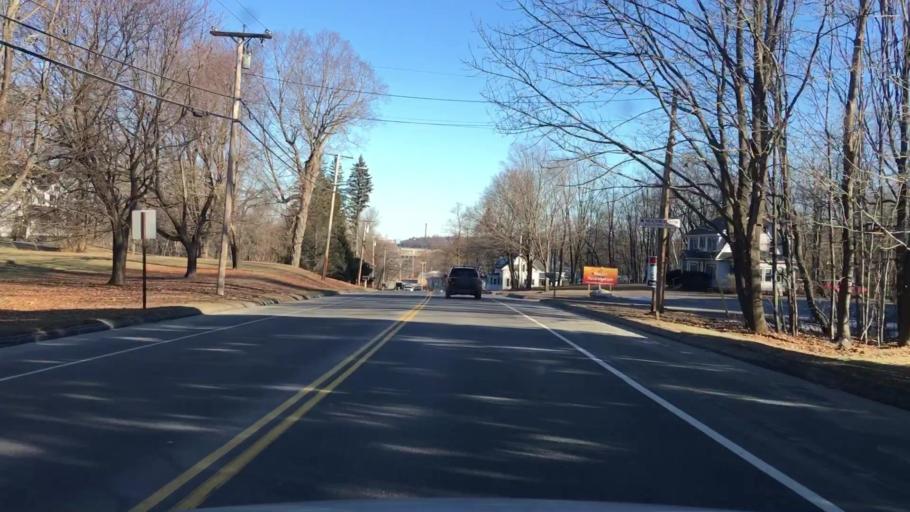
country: US
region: Maine
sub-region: Kennebec County
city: Waterville
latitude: 44.5316
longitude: -69.6380
